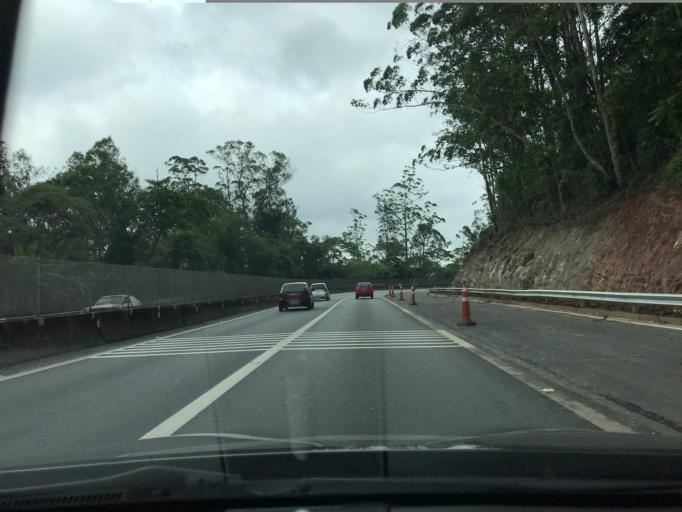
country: BR
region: Sao Paulo
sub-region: Cotia
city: Cotia
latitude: -23.6146
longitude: -46.9620
